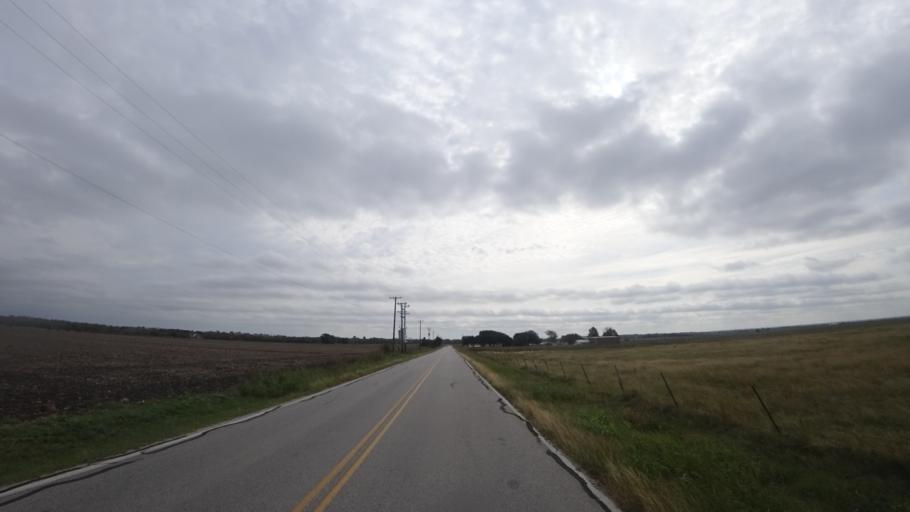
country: US
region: Texas
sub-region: Travis County
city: Manor
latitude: 30.4032
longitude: -97.5510
